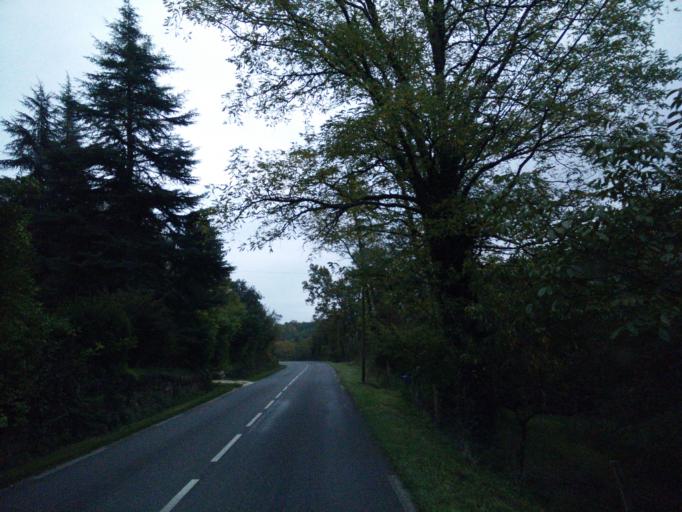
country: FR
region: Aquitaine
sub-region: Departement de la Dordogne
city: Carsac-Aillac
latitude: 44.7870
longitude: 1.3126
